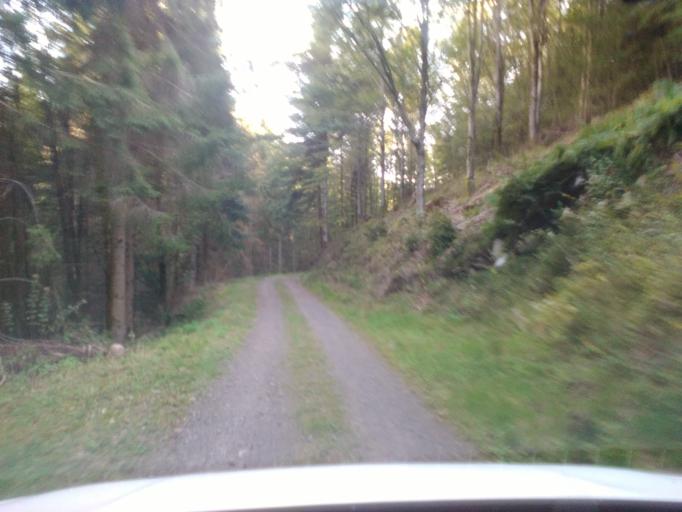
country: FR
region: Lorraine
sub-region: Departement des Vosges
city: Senones
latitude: 48.4342
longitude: 7.0349
